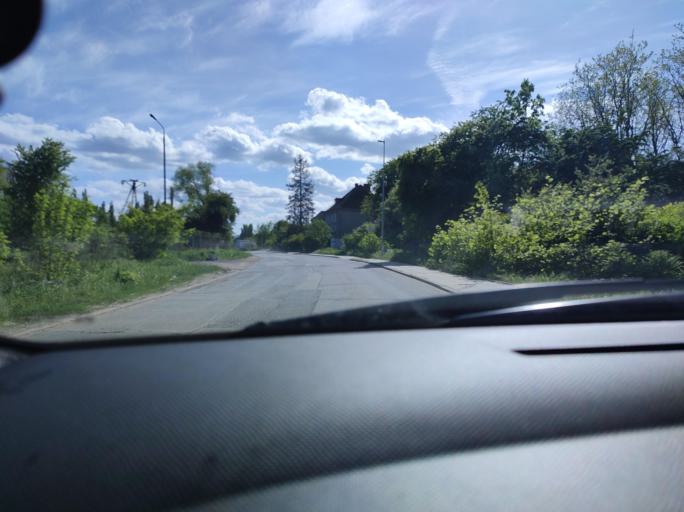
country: PL
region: West Pomeranian Voivodeship
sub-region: Powiat policki
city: Police
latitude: 53.5890
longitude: 14.5417
